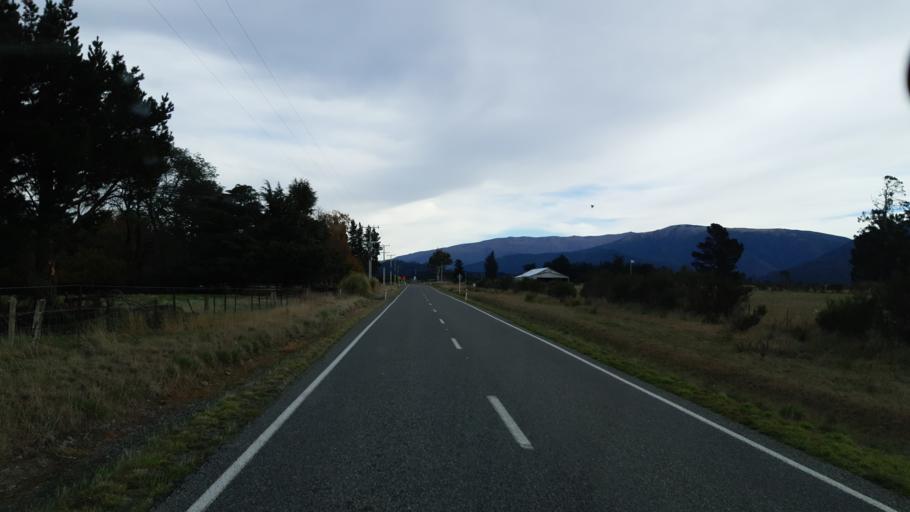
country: NZ
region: Tasman
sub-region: Tasman District
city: Brightwater
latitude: -41.6521
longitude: 173.2832
